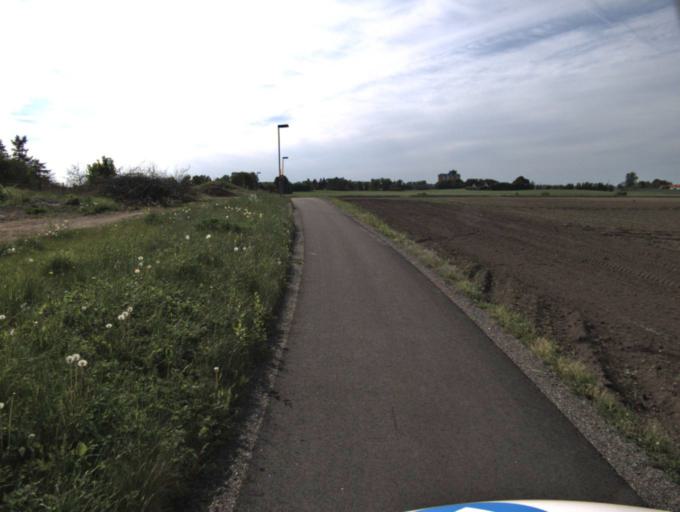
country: SE
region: Skane
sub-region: Kristianstads Kommun
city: Kristianstad
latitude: 56.0534
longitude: 14.1939
